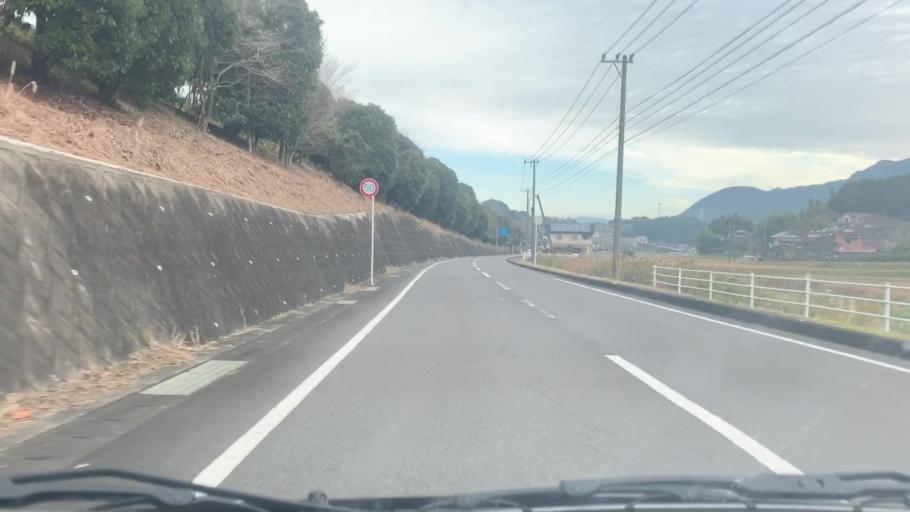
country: JP
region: Saga Prefecture
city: Ureshinomachi-shimojuku
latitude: 33.1236
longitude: 129.9805
